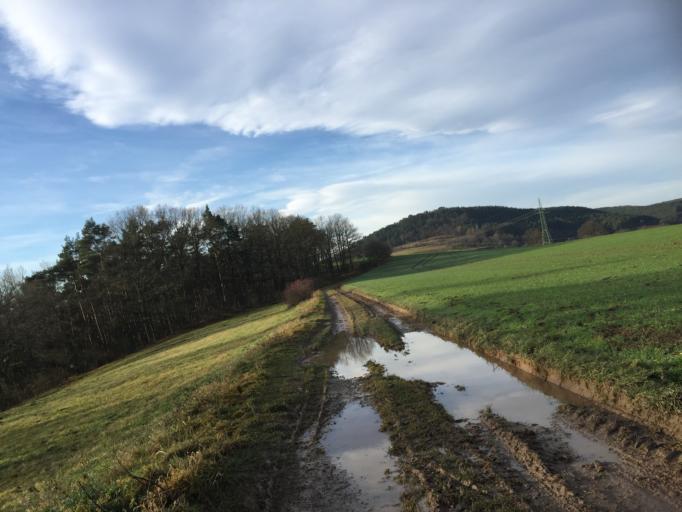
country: DE
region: Thuringia
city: Orlamunde
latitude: 50.7840
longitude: 11.5207
